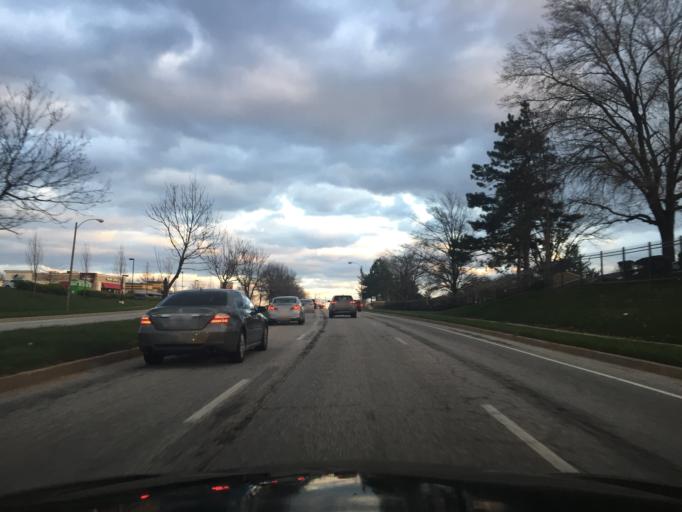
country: US
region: Maryland
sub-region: Baltimore County
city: Towson
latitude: 39.3978
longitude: -76.5863
